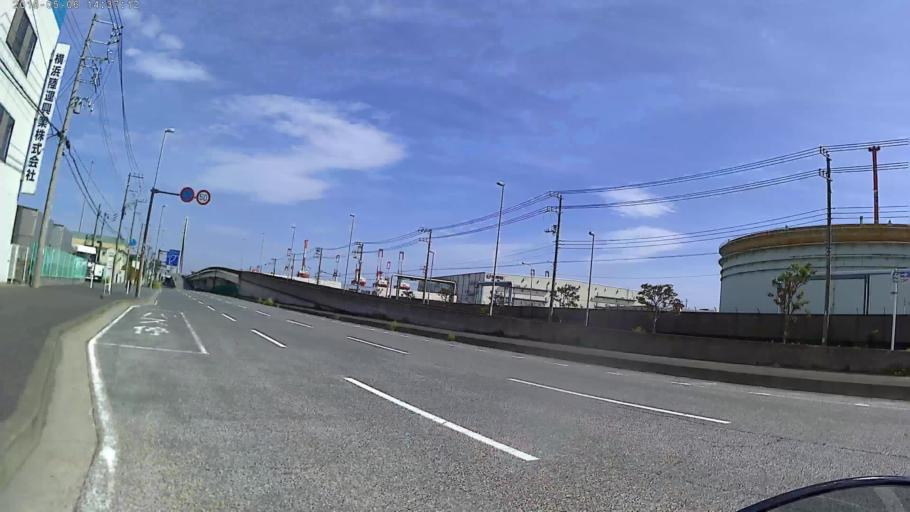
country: JP
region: Kanagawa
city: Yokohama
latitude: 35.4125
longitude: 139.6735
